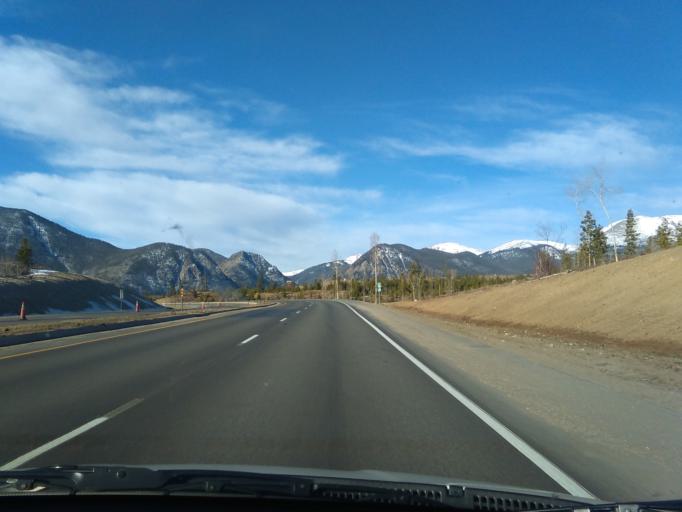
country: US
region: Colorado
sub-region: Summit County
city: Frisco
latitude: 39.5742
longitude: -106.0614
